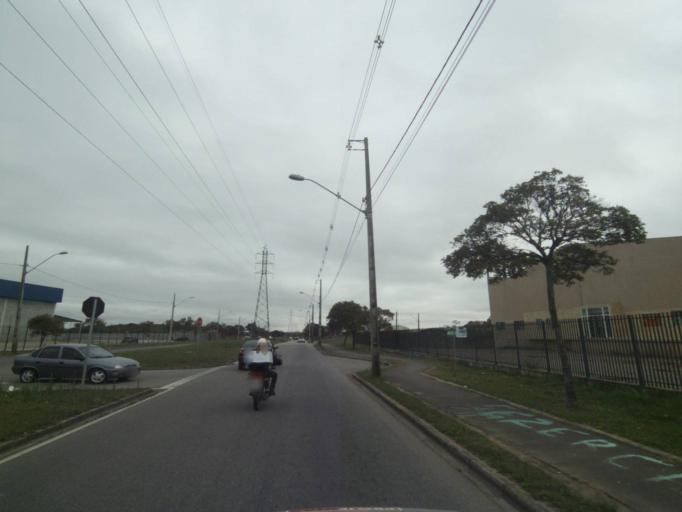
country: BR
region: Parana
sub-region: Sao Jose Dos Pinhais
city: Sao Jose dos Pinhais
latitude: -25.5040
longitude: -49.2123
